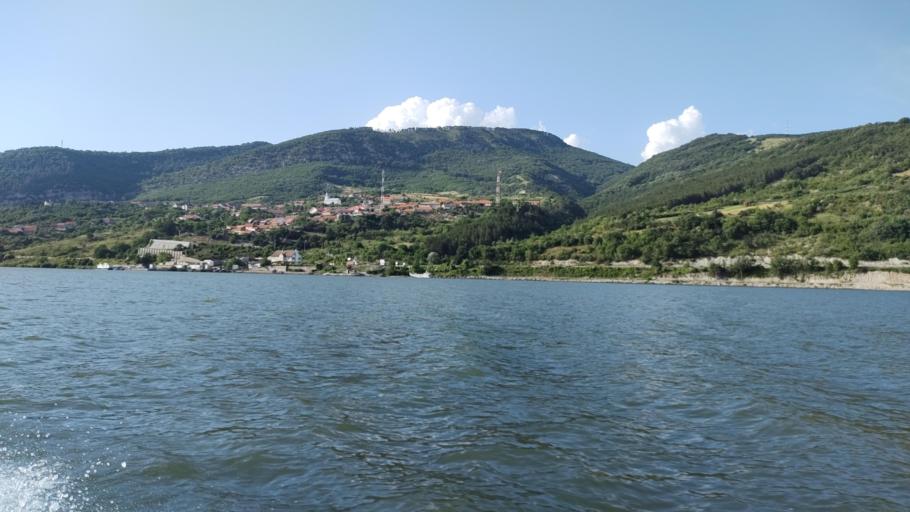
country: RO
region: Mehedinti
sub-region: Comuna Svinita
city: Svinita
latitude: 44.4905
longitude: 22.1066
